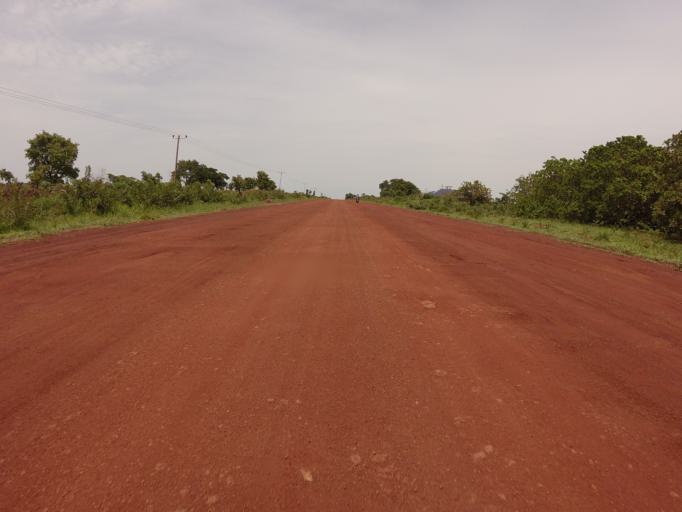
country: GH
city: Kpandae
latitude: 8.8265
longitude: 0.0617
